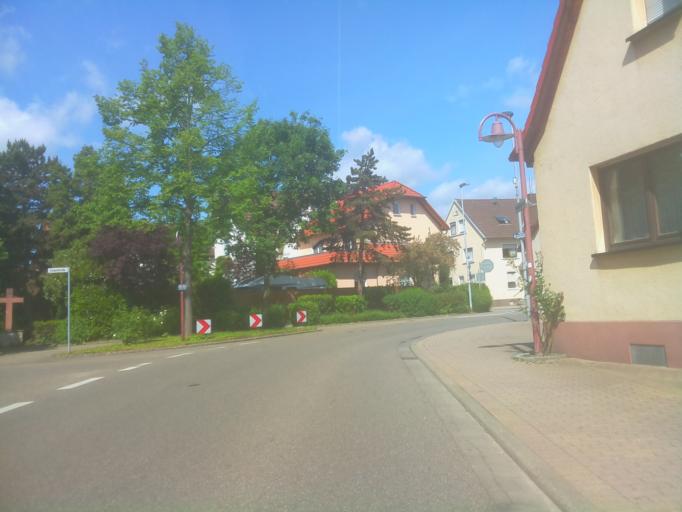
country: DE
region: Baden-Wuerttemberg
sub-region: Karlsruhe Region
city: Heddesheim
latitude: 49.5049
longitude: 8.5994
